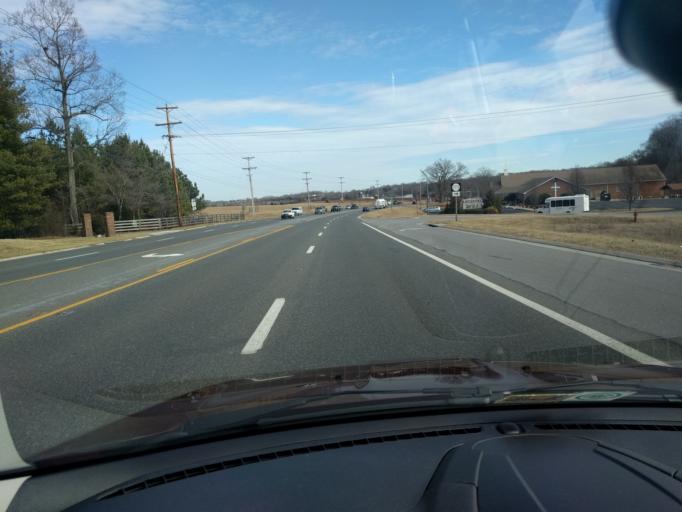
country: US
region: Virginia
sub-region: Bedford County
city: Forest
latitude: 37.3657
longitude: -79.2835
